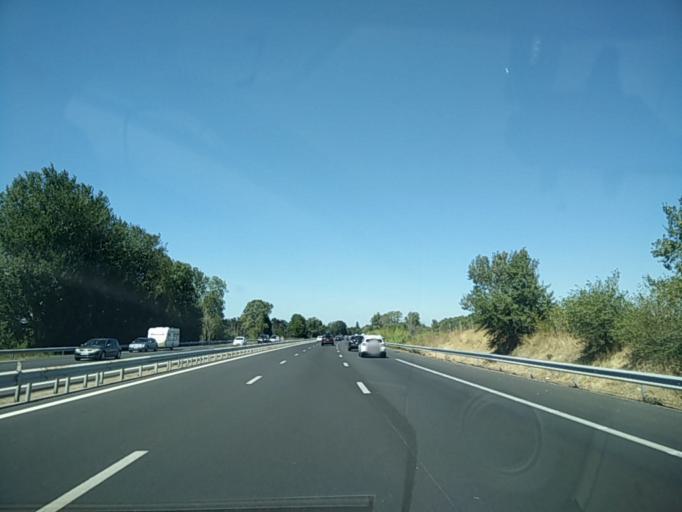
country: FR
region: Provence-Alpes-Cote d'Azur
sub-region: Departement du Vaucluse
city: Cavaillon
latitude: 43.8372
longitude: 4.9989
